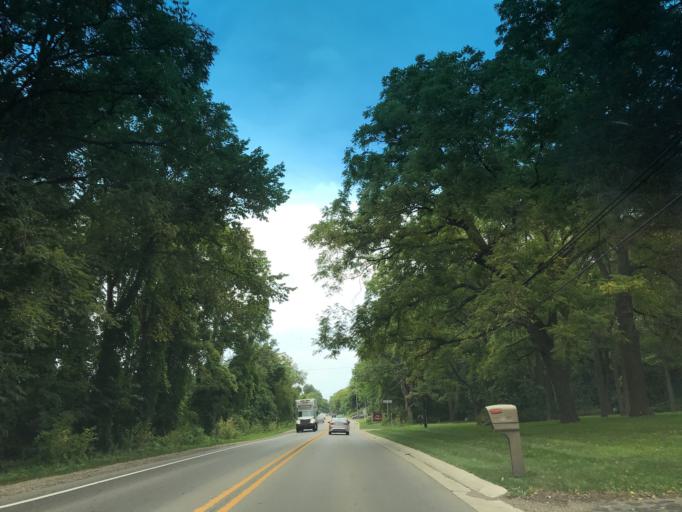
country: US
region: Michigan
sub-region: Oakland County
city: Milford
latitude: 42.5715
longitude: -83.6139
